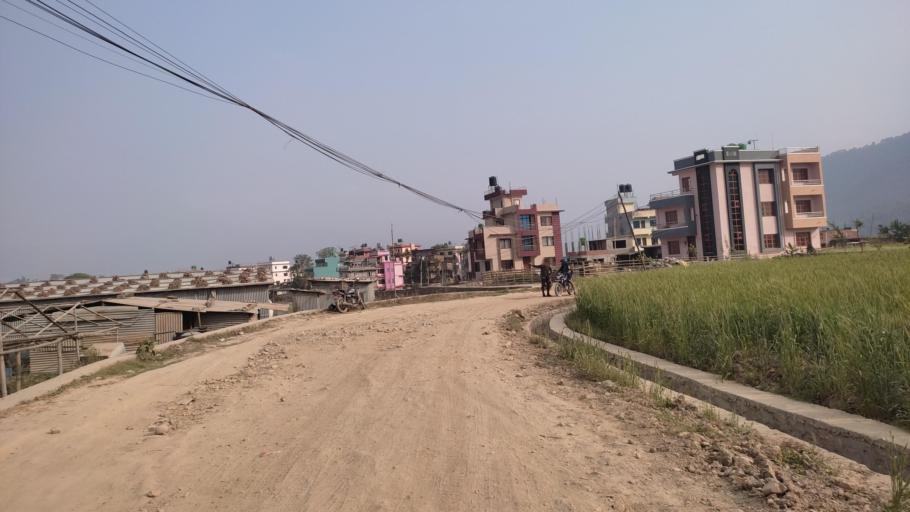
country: NP
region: Central Region
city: Kirtipur
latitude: 27.6640
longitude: 85.2767
